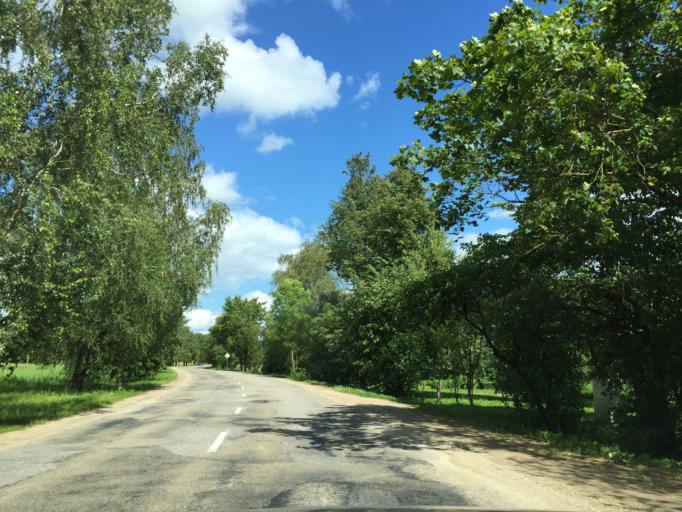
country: LV
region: Malpils
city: Malpils
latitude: 56.9010
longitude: 24.9215
